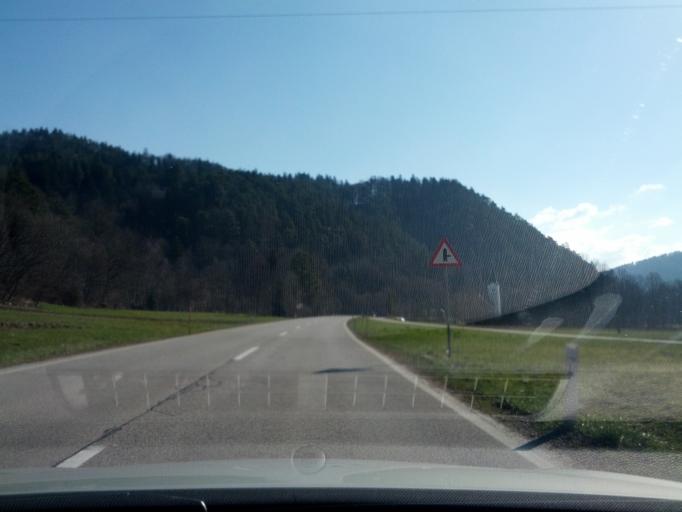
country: SI
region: Moravce
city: Moravce
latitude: 46.0962
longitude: 14.6874
